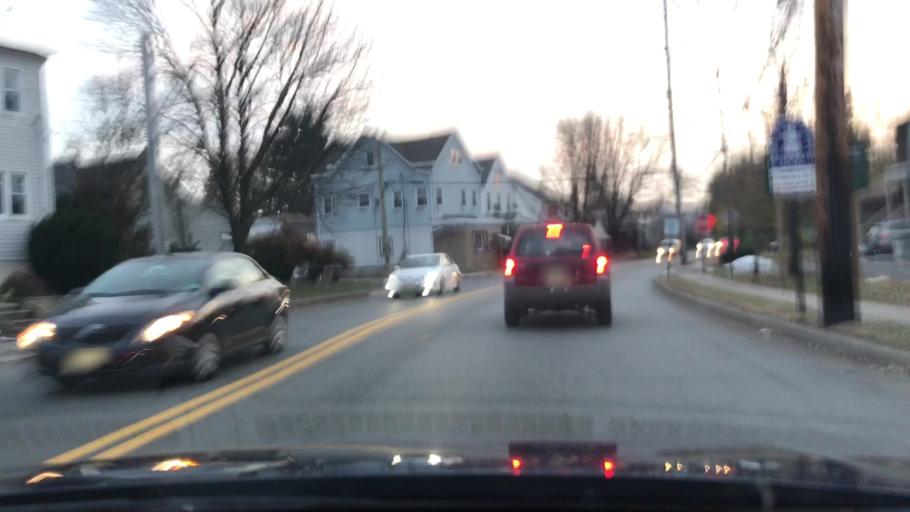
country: US
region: New Jersey
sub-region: Bergen County
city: Wallington
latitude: 40.8580
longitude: -74.1058
